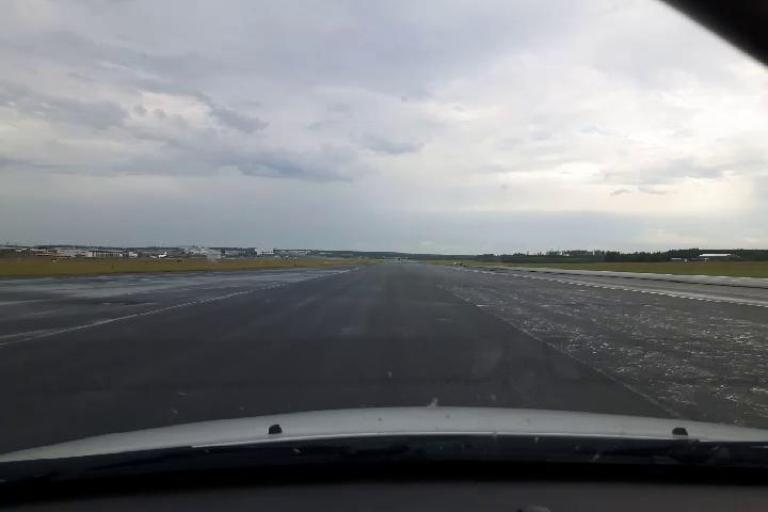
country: SE
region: Stockholm
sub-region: Sigtuna Kommun
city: Rosersberg
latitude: 59.6318
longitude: 17.9524
